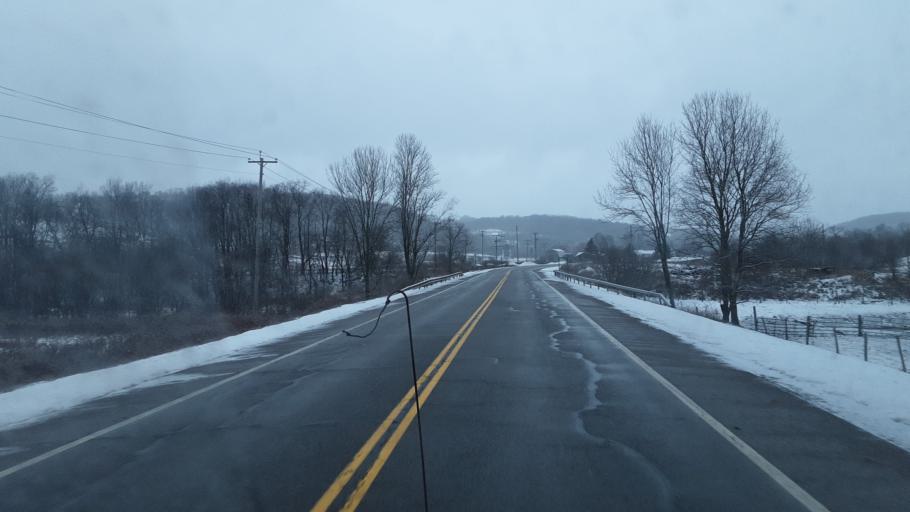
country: US
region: Pennsylvania
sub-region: Tioga County
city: Westfield
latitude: 42.0638
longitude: -77.5520
